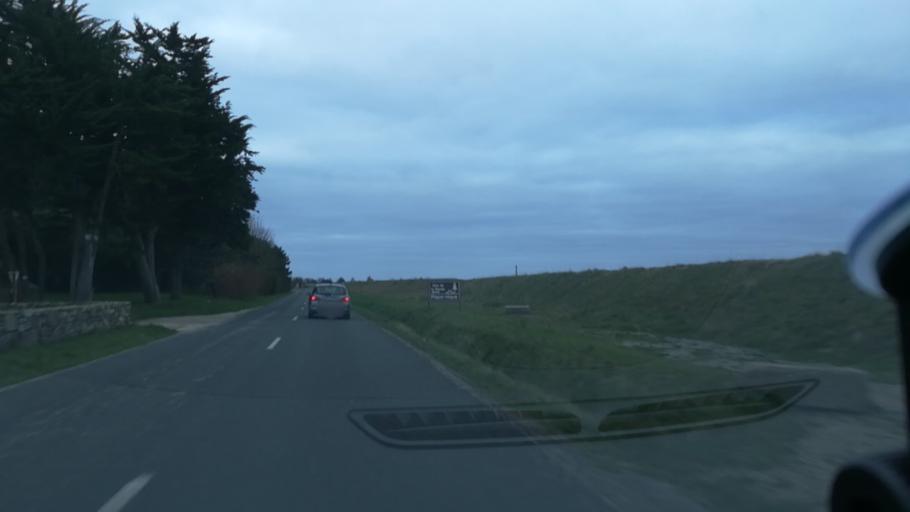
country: FR
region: Lower Normandy
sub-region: Departement de la Manche
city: Saint-Vaast-la-Hougue
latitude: 49.6008
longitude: -1.2615
